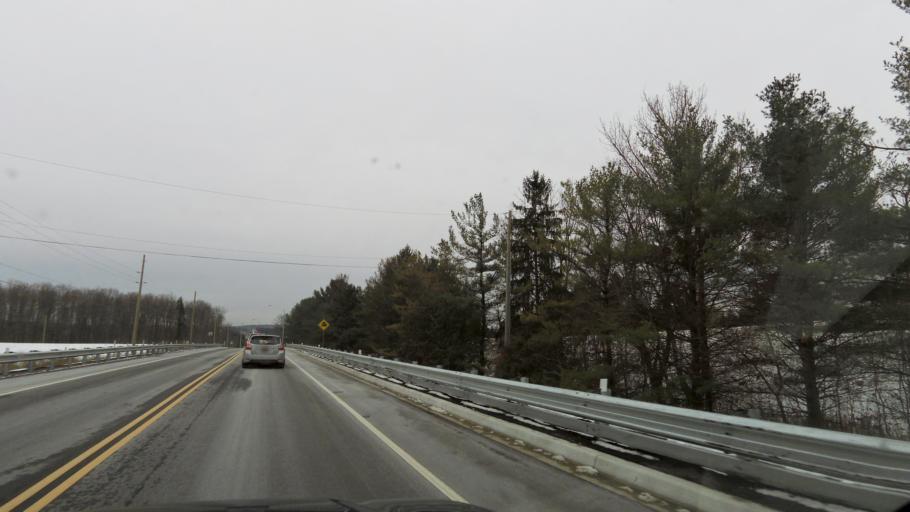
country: CA
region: Ontario
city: Newmarket
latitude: 44.0802
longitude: -79.5140
